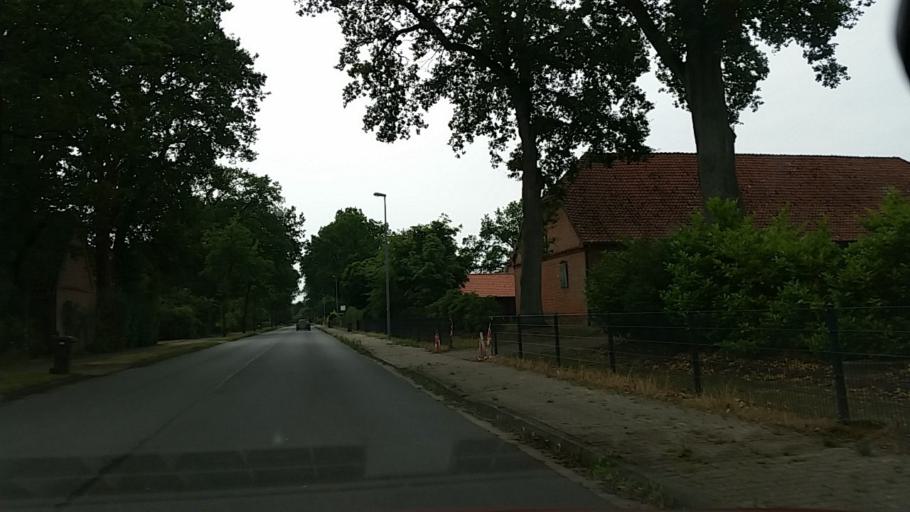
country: DE
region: Lower Saxony
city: Eickeloh
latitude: 52.7337
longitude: 9.6032
